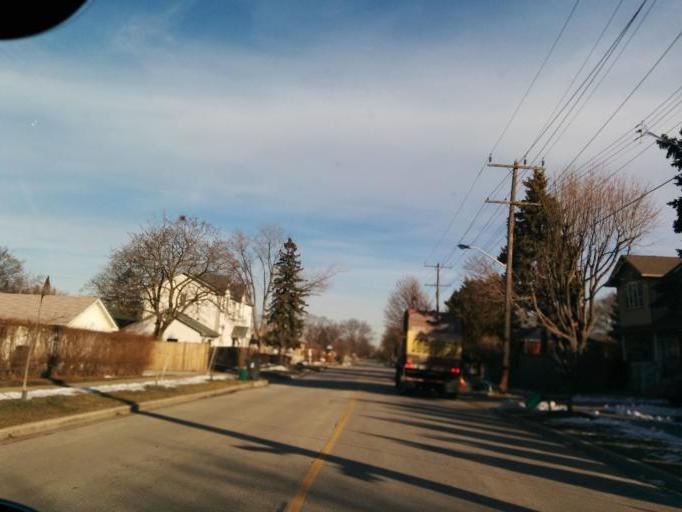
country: CA
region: Ontario
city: Etobicoke
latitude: 43.6081
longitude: -79.5378
